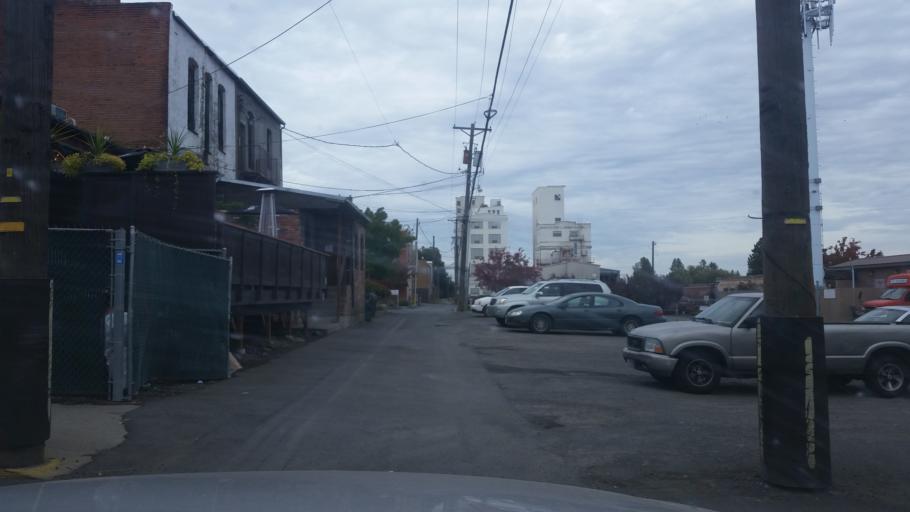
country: US
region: Washington
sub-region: Spokane County
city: Cheney
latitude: 47.4866
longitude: -117.5755
